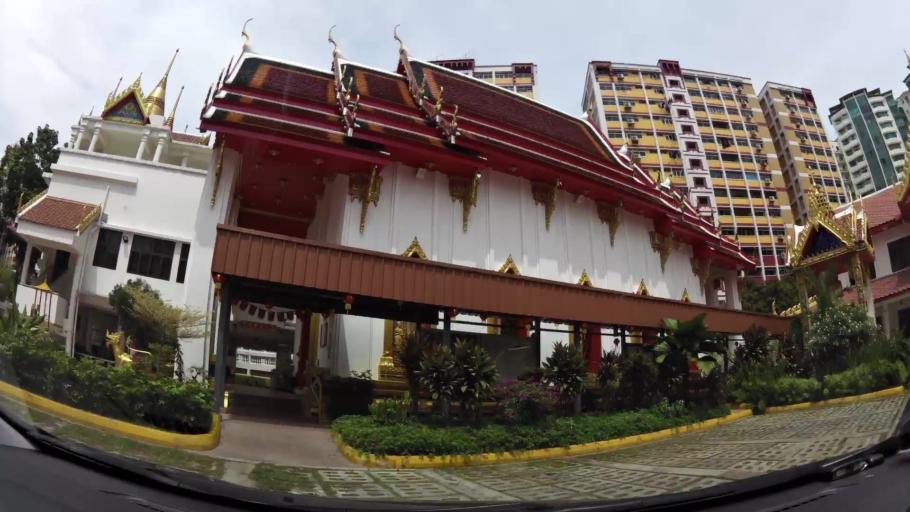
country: MY
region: Johor
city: Johor Bahru
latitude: 1.3786
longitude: 103.7455
